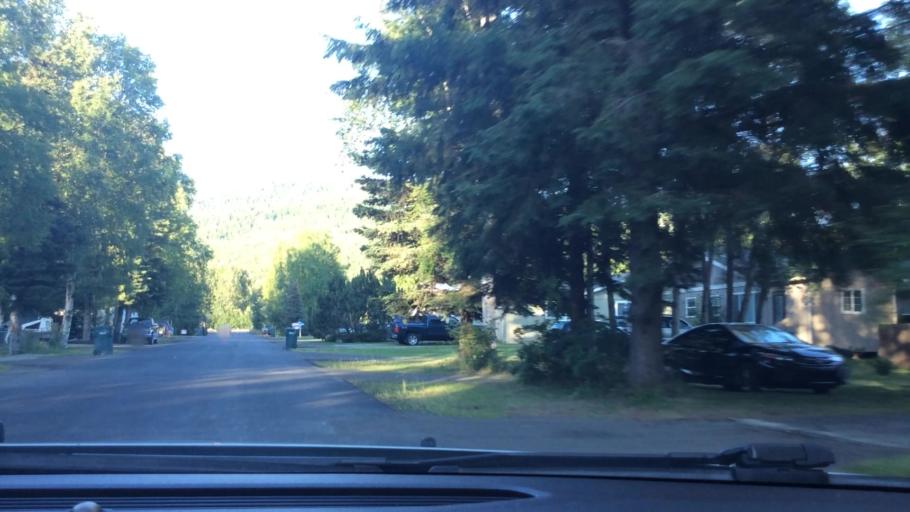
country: US
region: Alaska
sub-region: Anchorage Municipality
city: Eagle River
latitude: 61.3374
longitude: -149.5680
